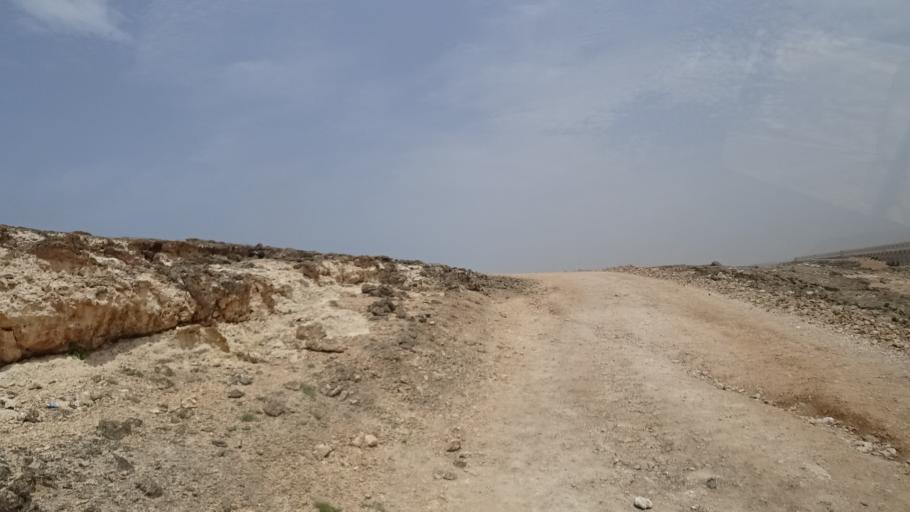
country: OM
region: Zufar
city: Salalah
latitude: 17.0363
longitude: 54.4104
